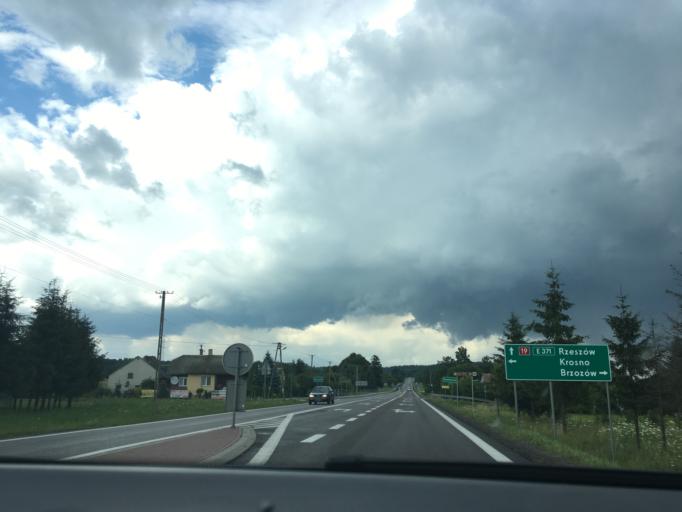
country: PL
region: Subcarpathian Voivodeship
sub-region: Powiat brzozowski
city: Jablonica Polska
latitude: 49.6992
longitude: 21.8794
